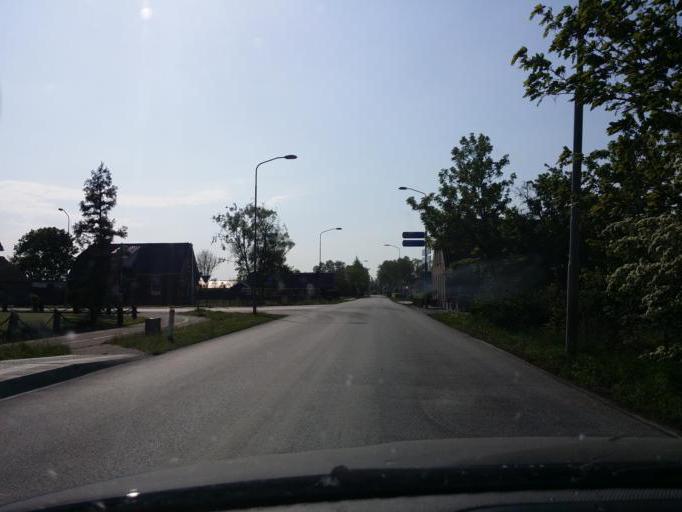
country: NL
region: Groningen
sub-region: Gemeente Zuidhorn
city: Grijpskerk
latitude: 53.2213
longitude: 6.3222
